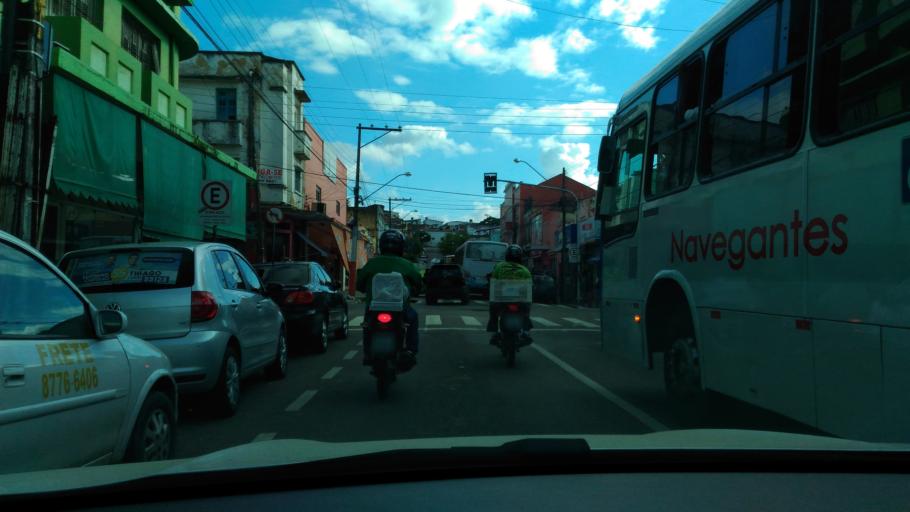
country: BR
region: Paraiba
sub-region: Joao Pessoa
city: Joao Pessoa
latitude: -7.1204
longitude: -34.8872
